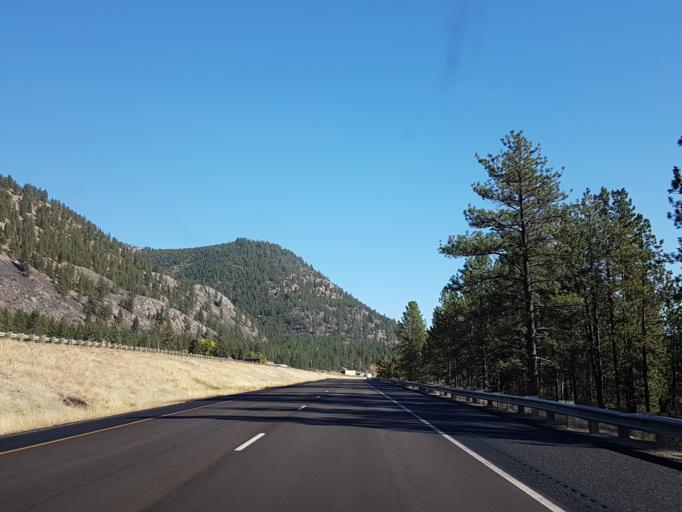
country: US
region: Montana
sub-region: Missoula County
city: Frenchtown
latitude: 47.0195
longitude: -114.5177
